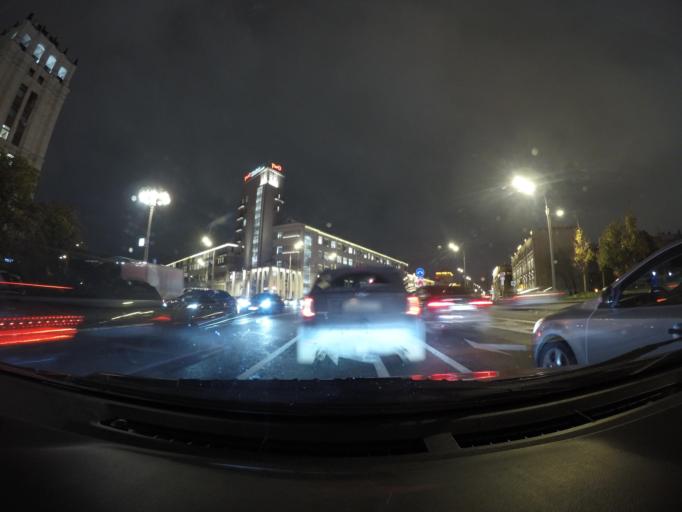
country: RU
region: Moscow
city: Moscow
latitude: 55.7687
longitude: 37.6493
